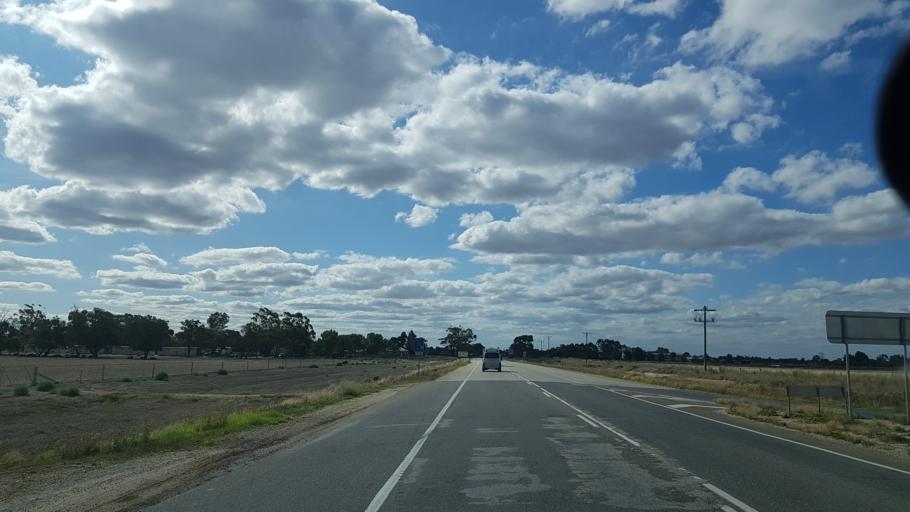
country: AU
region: Victoria
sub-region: Swan Hill
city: Swan Hill
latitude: -35.7630
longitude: 143.9311
